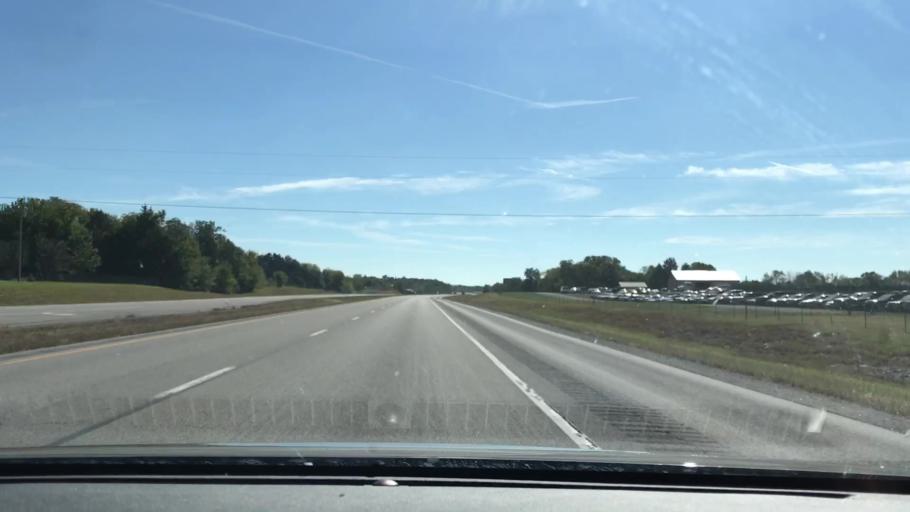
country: US
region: Kentucky
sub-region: Todd County
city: Elkton
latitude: 36.8361
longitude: -87.2375
